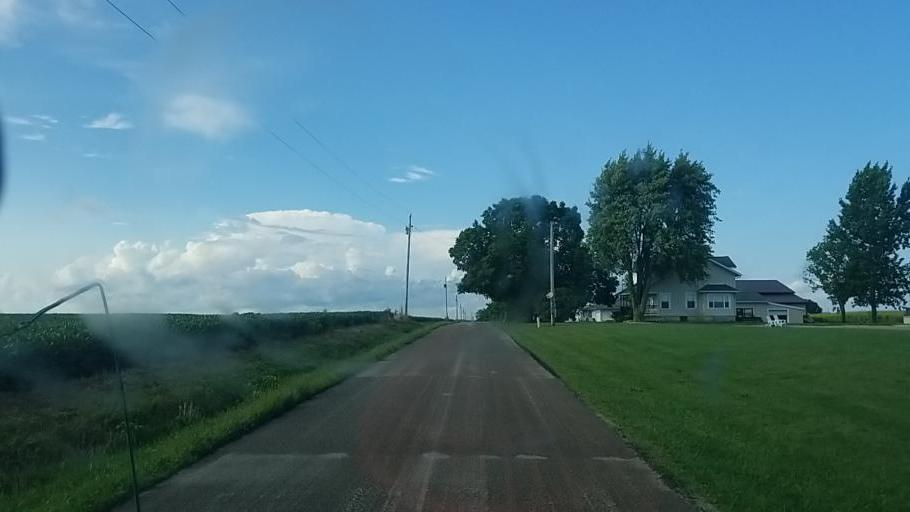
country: US
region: Ohio
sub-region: Wyandot County
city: Upper Sandusky
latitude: 40.8080
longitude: -83.3041
